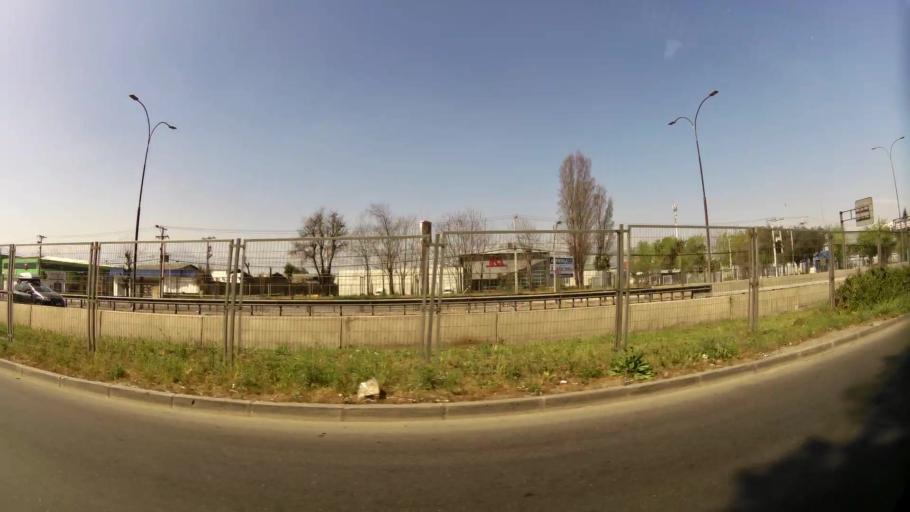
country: CL
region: Santiago Metropolitan
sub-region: Provincia de Santiago
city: Santiago
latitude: -33.4113
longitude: -70.6799
